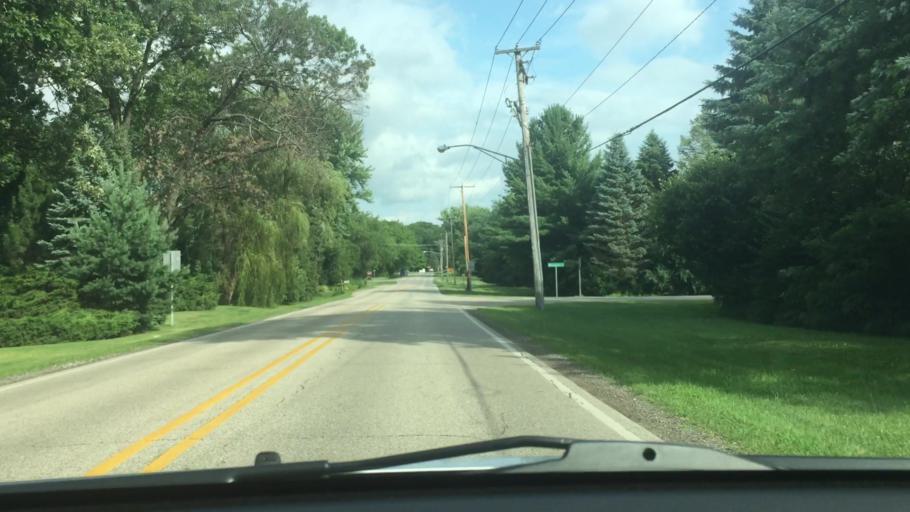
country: US
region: Illinois
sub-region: McHenry County
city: Crystal Lake
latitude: 42.2647
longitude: -88.3388
